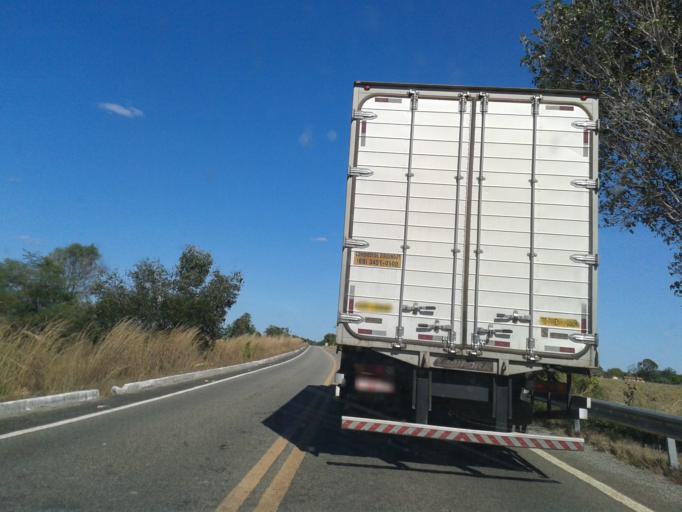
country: BR
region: Goias
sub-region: Sao Miguel Do Araguaia
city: Sao Miguel do Araguaia
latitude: -13.6111
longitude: -50.3206
